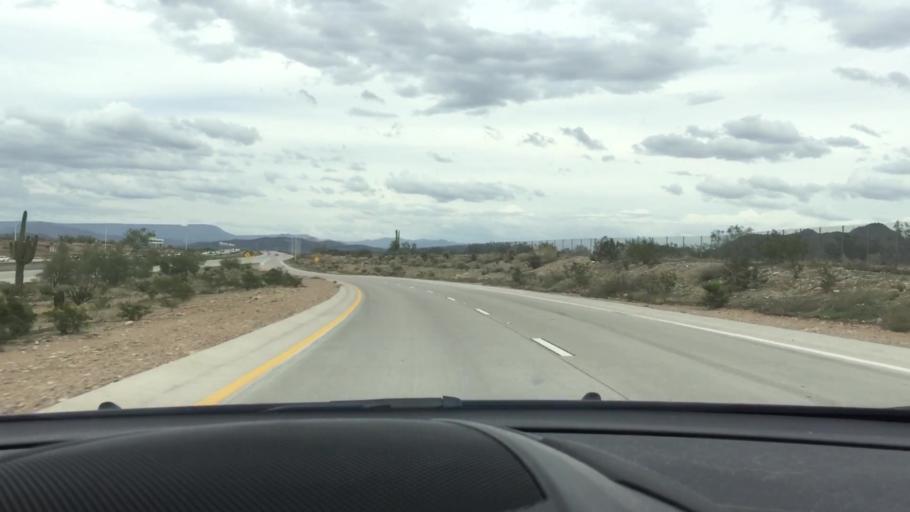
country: US
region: Arizona
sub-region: Maricopa County
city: Anthem
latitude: 33.7697
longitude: -112.2486
